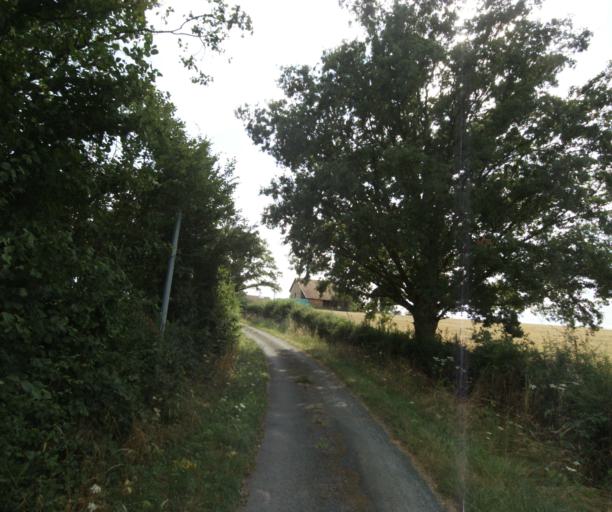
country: FR
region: Bourgogne
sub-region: Departement de Saone-et-Loire
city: Gueugnon
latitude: 46.6071
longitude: 4.0883
